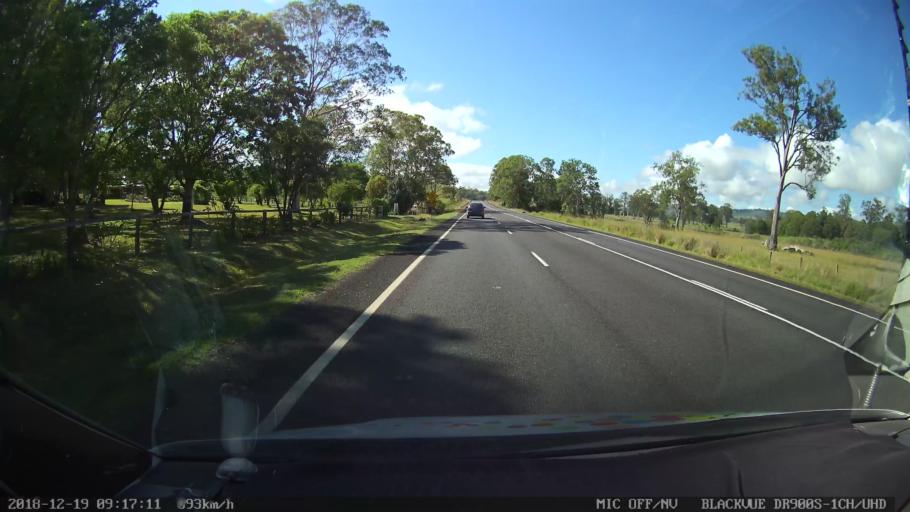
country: AU
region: New South Wales
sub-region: Kyogle
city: Kyogle
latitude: -28.5301
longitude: 152.9728
